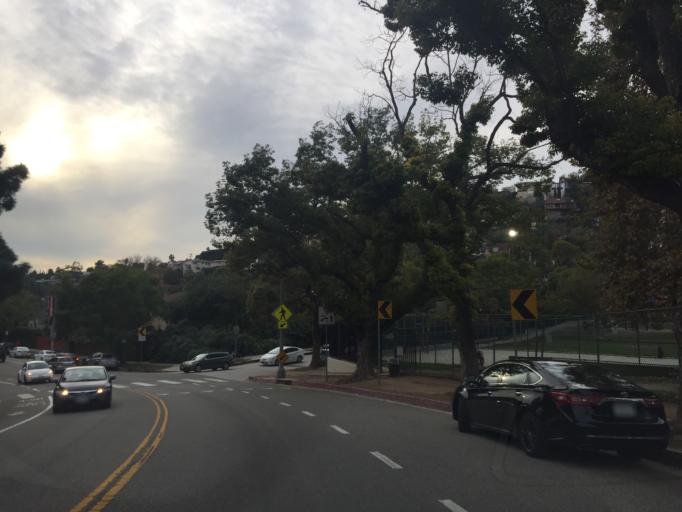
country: US
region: California
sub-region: Los Angeles County
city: Silver Lake
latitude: 34.0920
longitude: -118.2655
